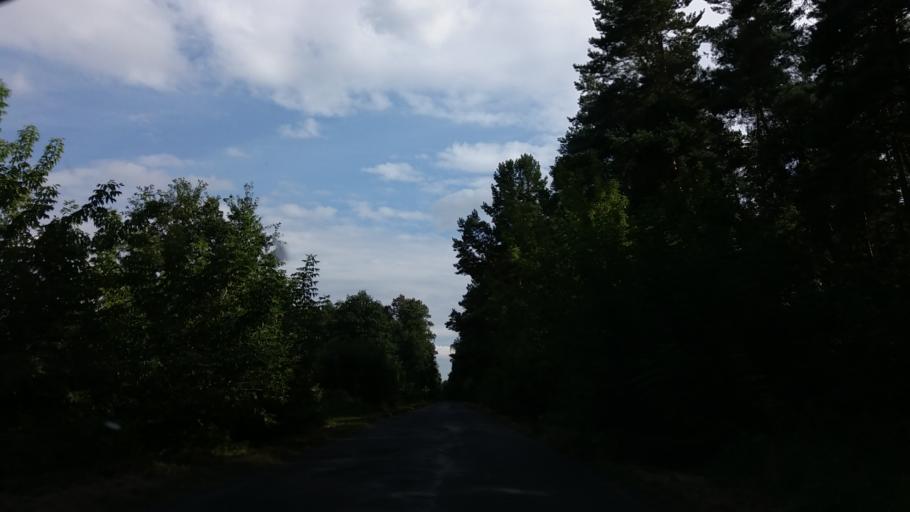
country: PL
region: West Pomeranian Voivodeship
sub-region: Powiat stargardzki
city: Dolice
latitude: 53.2378
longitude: 15.2492
